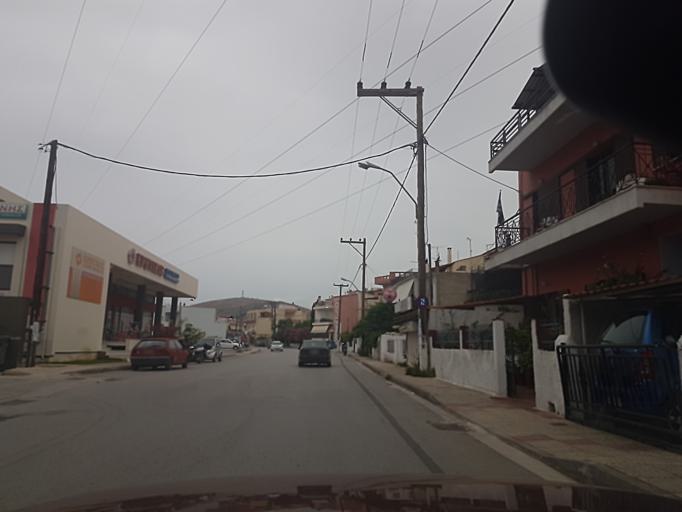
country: GR
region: Central Greece
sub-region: Nomos Evvoias
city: Chalkida
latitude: 38.4676
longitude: 23.6208
